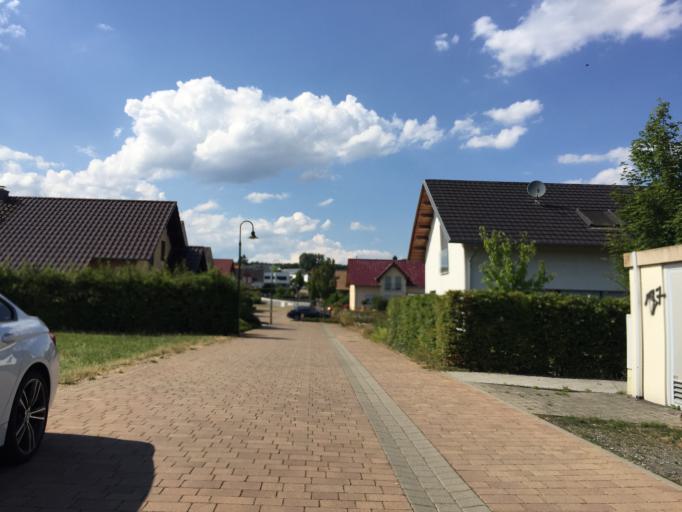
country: DE
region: Hesse
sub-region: Regierungsbezirk Giessen
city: Heuchelheim
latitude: 50.6260
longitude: 8.6432
